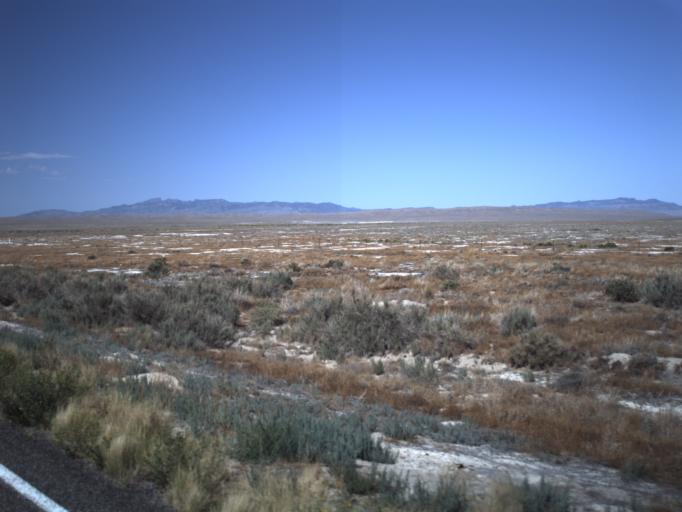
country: US
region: Utah
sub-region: Millard County
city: Delta
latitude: 39.2125
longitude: -112.9625
